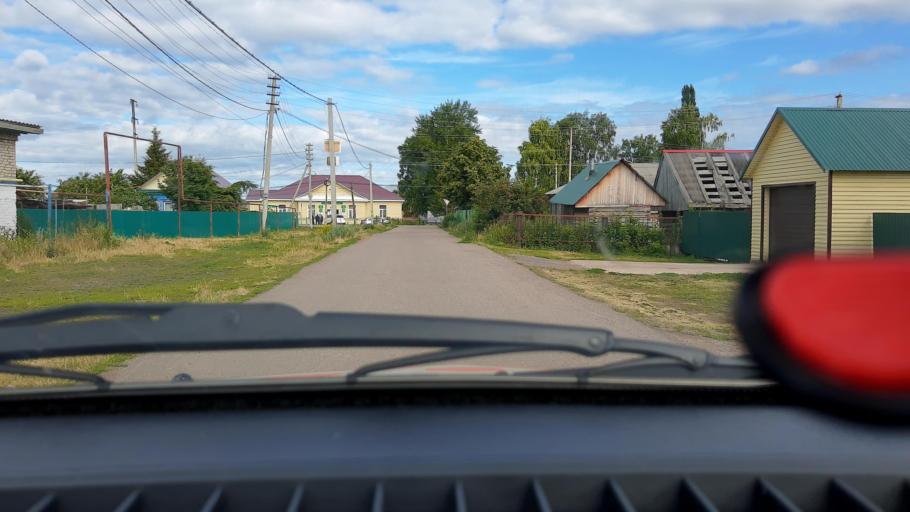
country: RU
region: Bashkortostan
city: Kabakovo
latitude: 54.5168
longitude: 55.9473
